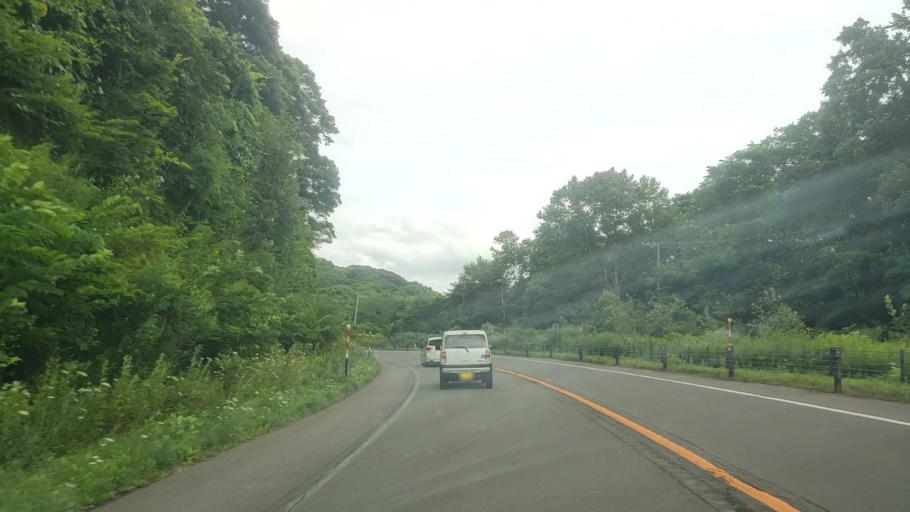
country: JP
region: Hokkaido
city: Nanae
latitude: 41.9697
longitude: 140.6512
